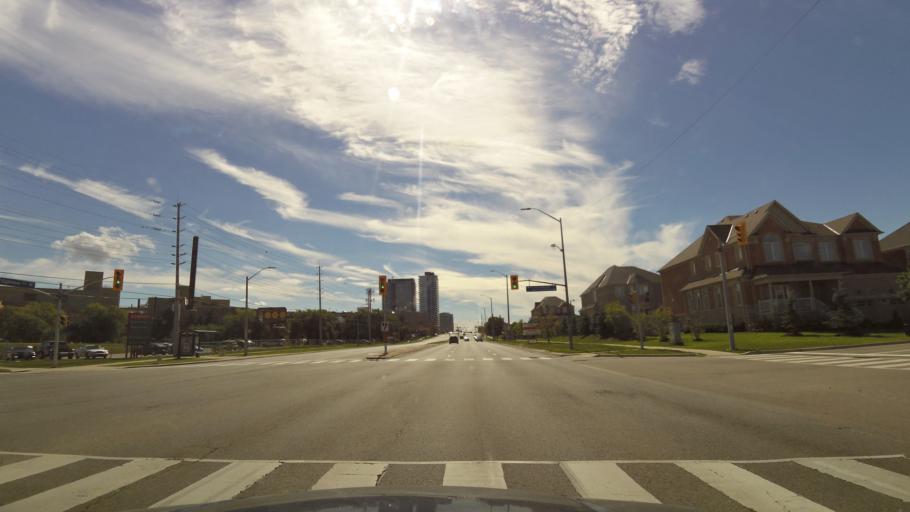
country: CA
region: Ontario
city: Mississauga
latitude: 43.5625
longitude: -79.7029
